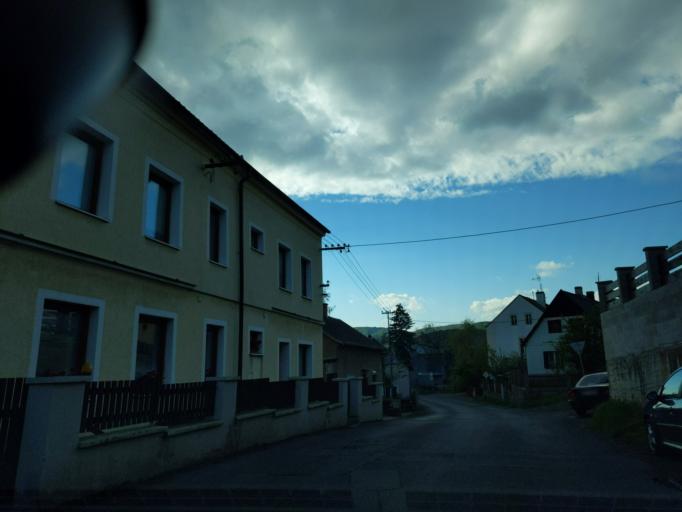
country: CZ
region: Ustecky
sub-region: Okres Usti nad Labem
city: Usti nad Labem
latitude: 50.6893
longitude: 14.0067
